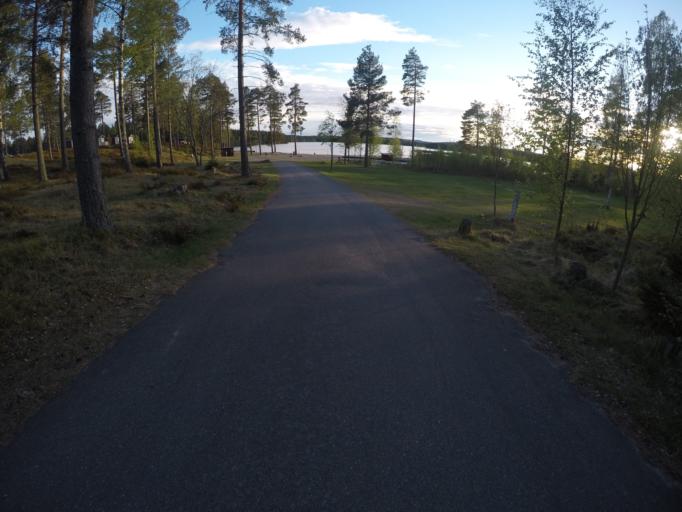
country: SE
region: Gaevleborg
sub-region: Hudiksvalls Kommun
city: Iggesund
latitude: 61.6591
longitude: 17.0790
